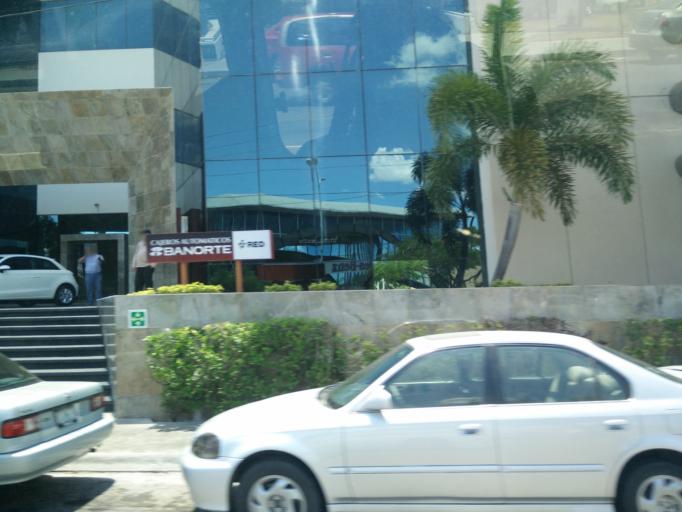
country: MX
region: Yucatan
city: Merida
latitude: 21.0240
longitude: -89.6226
